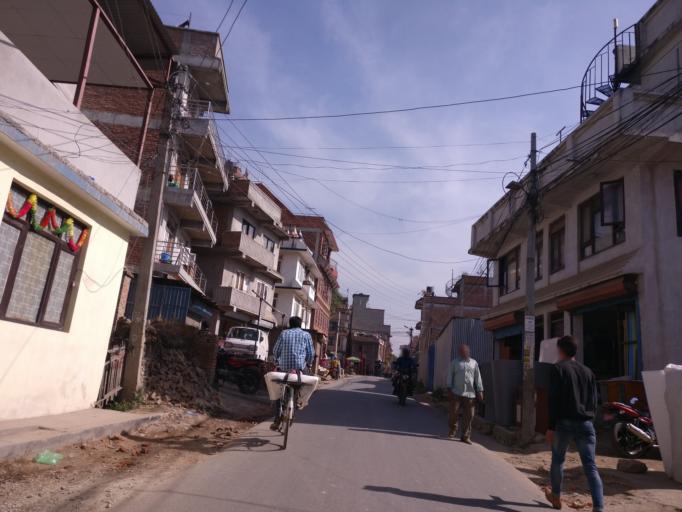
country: NP
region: Central Region
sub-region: Bagmati Zone
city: Patan
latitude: 27.6739
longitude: 85.3310
